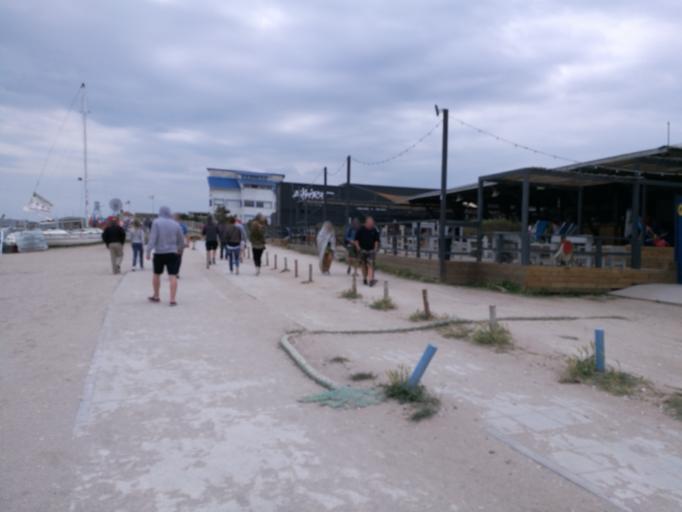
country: RO
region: Constanta
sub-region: Municipiul Mangalia
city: Mangalia
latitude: 43.7499
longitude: 28.5771
